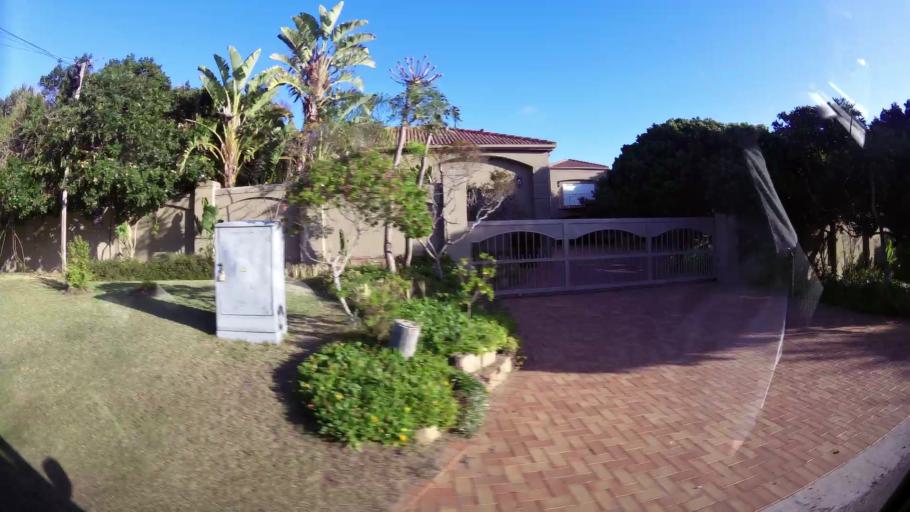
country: ZA
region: Western Cape
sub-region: Eden District Municipality
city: George
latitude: -34.0013
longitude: 22.6329
